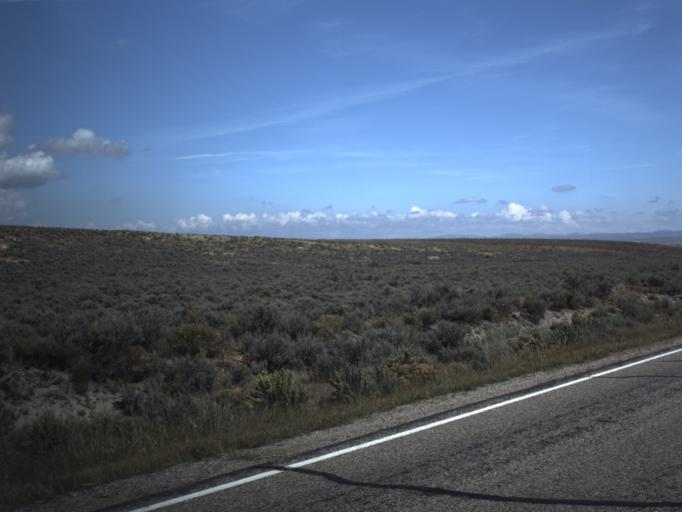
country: US
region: Utah
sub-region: Rich County
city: Randolph
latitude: 41.7714
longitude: -111.1347
